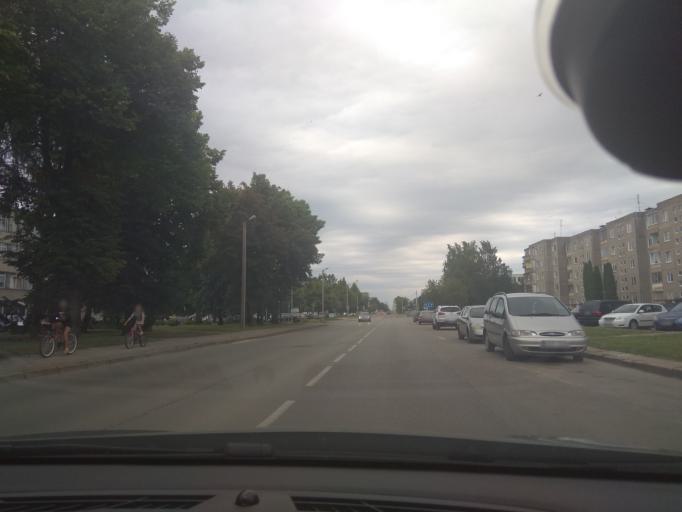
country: LT
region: Marijampoles apskritis
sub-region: Marijampole Municipality
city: Marijampole
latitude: 54.5676
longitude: 23.3662
